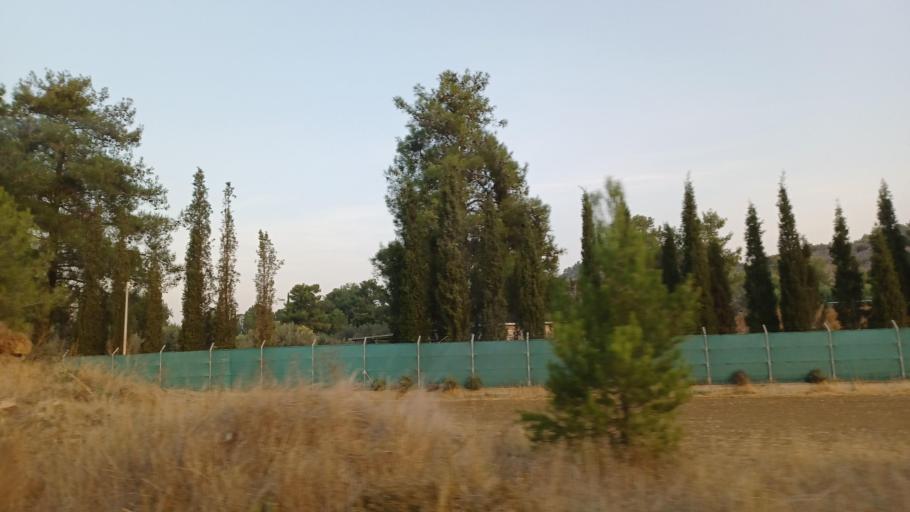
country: CY
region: Larnaka
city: Kornos
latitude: 34.9140
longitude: 33.3667
